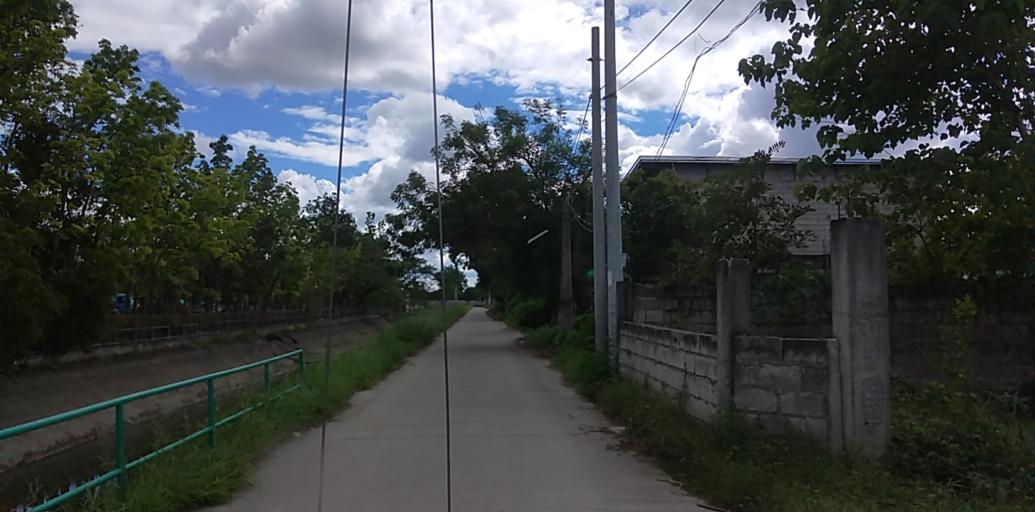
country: PH
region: Central Luzon
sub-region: Province of Pampanga
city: Arayat
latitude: 15.1395
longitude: 120.7783
